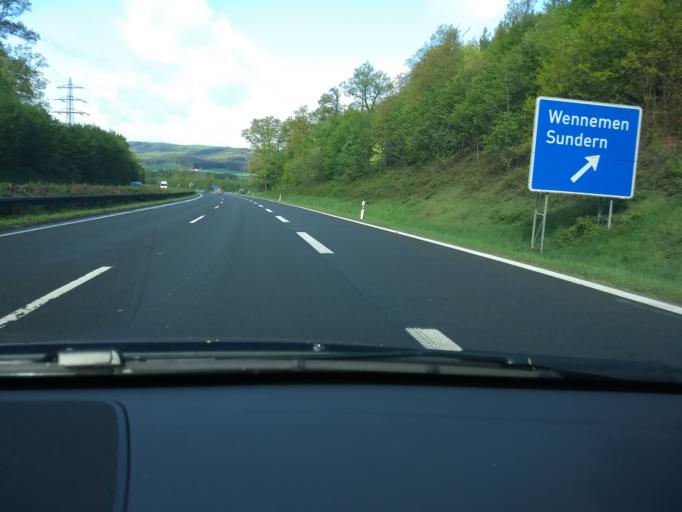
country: DE
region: North Rhine-Westphalia
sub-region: Regierungsbezirk Arnsberg
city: Meschede
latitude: 51.3603
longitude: 8.1943
